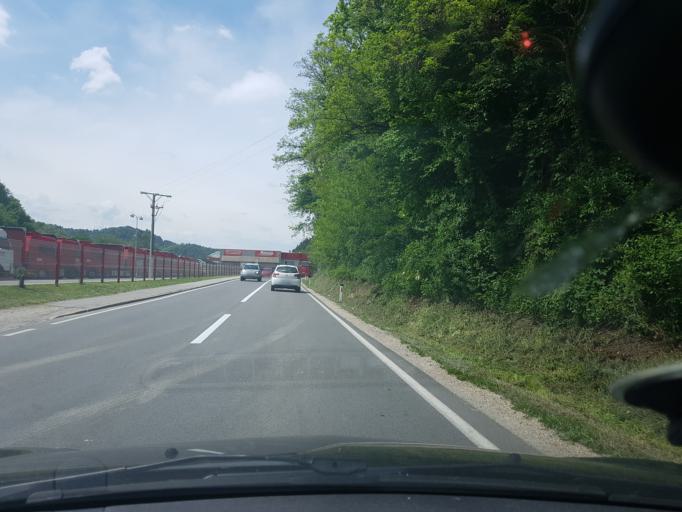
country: SI
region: Store
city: Store
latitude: 46.2226
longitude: 15.3186
